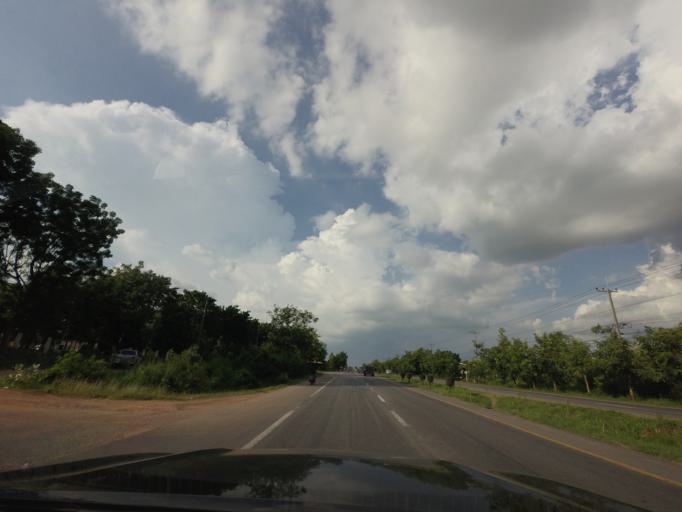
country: TH
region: Khon Kaen
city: Ban Haet
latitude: 16.2422
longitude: 102.7707
